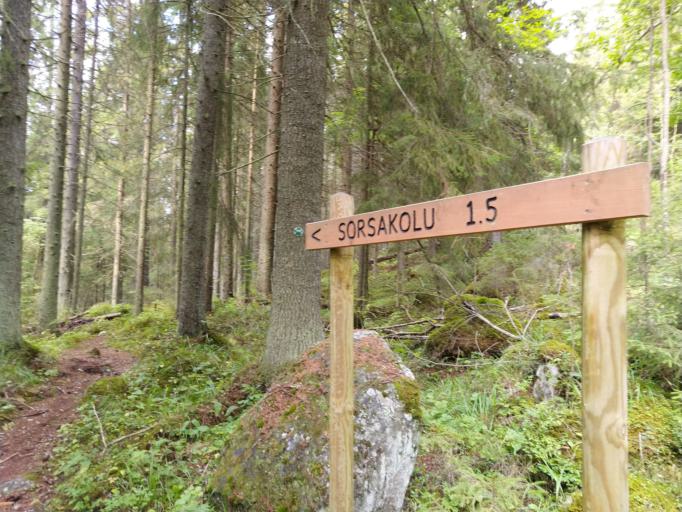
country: FI
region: Paijanne Tavastia
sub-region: Lahti
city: Auttoinen
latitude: 61.2290
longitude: 25.1671
